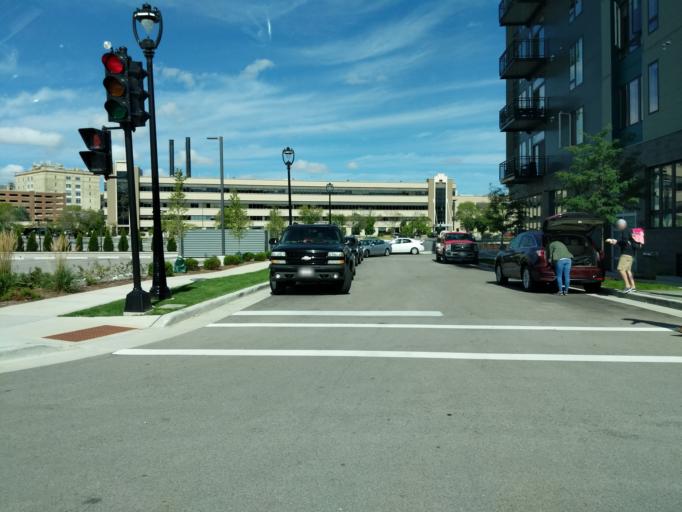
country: US
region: Wisconsin
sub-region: Milwaukee County
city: Milwaukee
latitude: 43.0490
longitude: -87.9091
